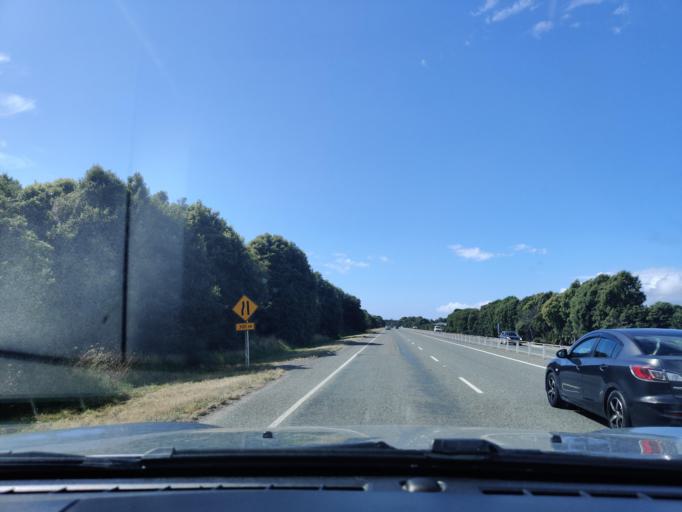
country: NZ
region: Tasman
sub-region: Tasman District
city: Richmond
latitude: -41.3110
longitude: 173.2176
